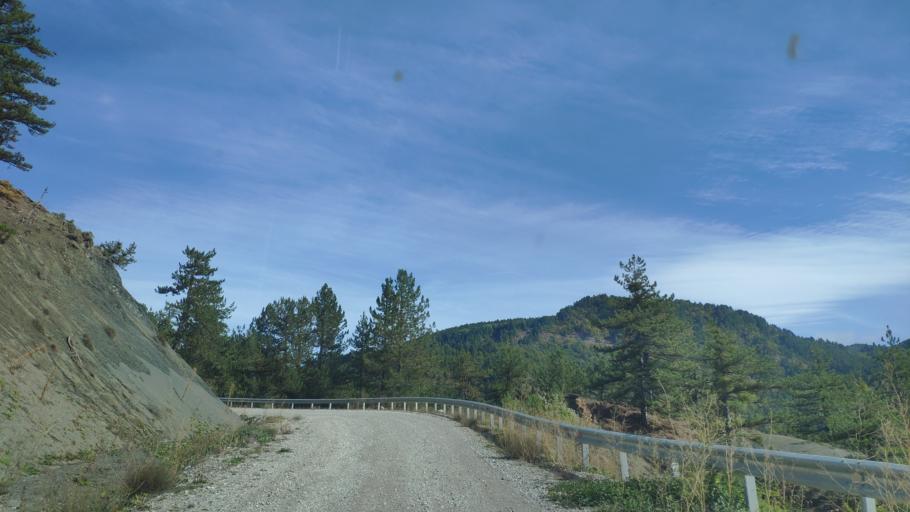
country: AL
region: Korce
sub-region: Rrethi i Devollit
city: Miras
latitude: 40.4180
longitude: 20.8700
